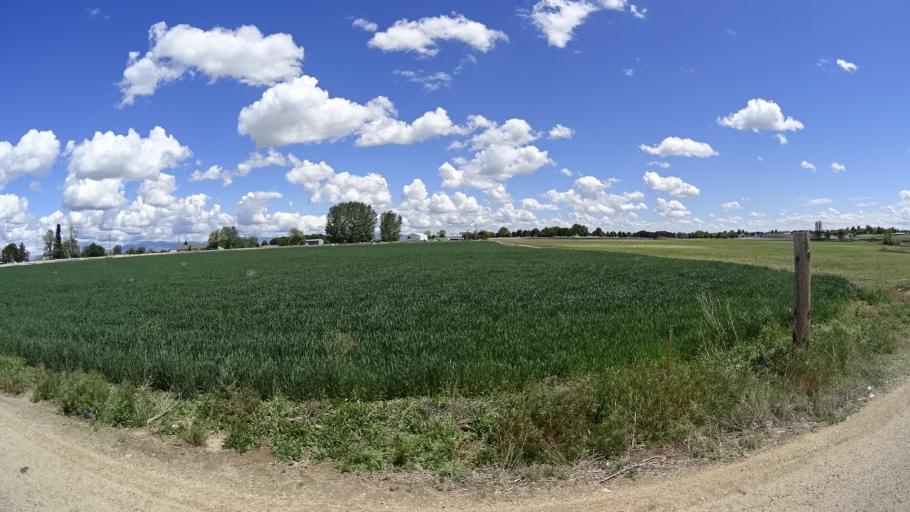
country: US
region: Idaho
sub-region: Ada County
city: Meridian
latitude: 43.5740
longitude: -116.4338
